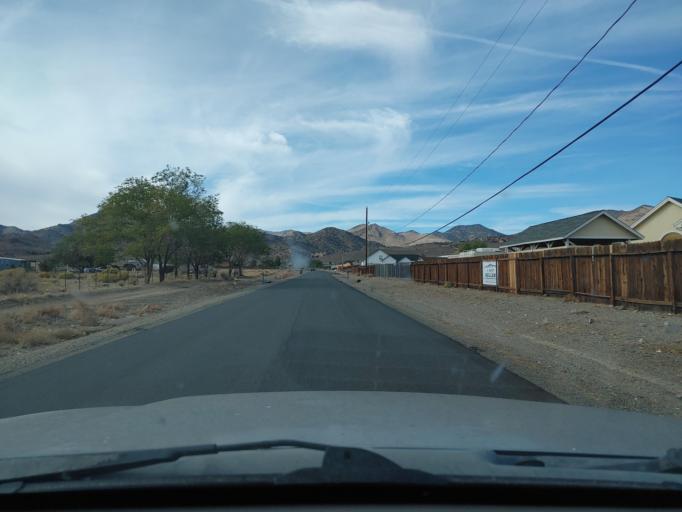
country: US
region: Nevada
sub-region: Lyon County
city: Dayton
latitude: 39.3036
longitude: -119.5473
